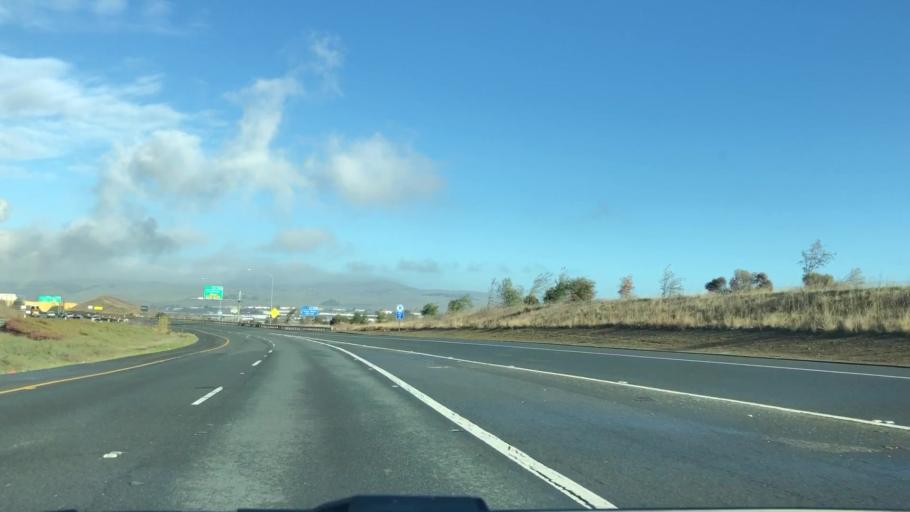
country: US
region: California
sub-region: Solano County
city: Benicia
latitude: 38.0558
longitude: -122.1294
